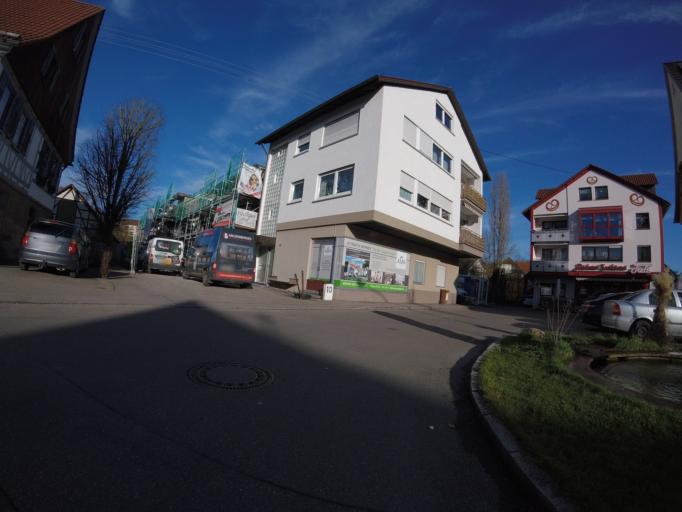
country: DE
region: Baden-Wuerttemberg
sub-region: Regierungsbezirk Stuttgart
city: Allmersbach im Tal
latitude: 48.9308
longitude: 9.4768
